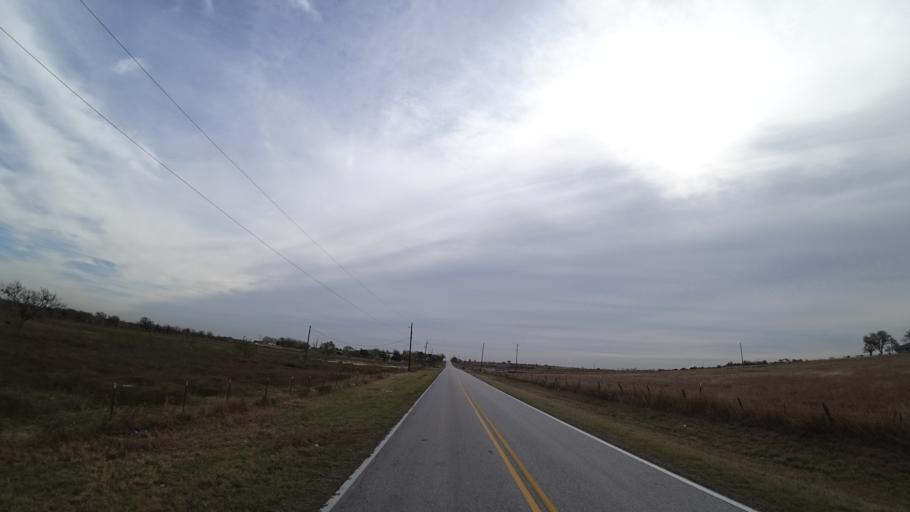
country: US
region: Texas
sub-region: Travis County
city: Onion Creek
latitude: 30.1398
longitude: -97.7240
